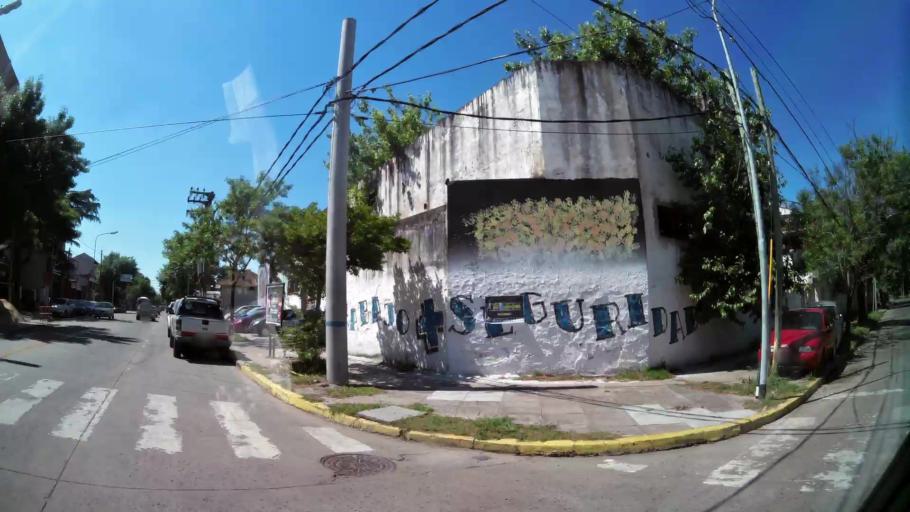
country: AR
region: Buenos Aires
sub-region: Partido de Tigre
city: Tigre
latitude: -34.4286
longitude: -58.5669
